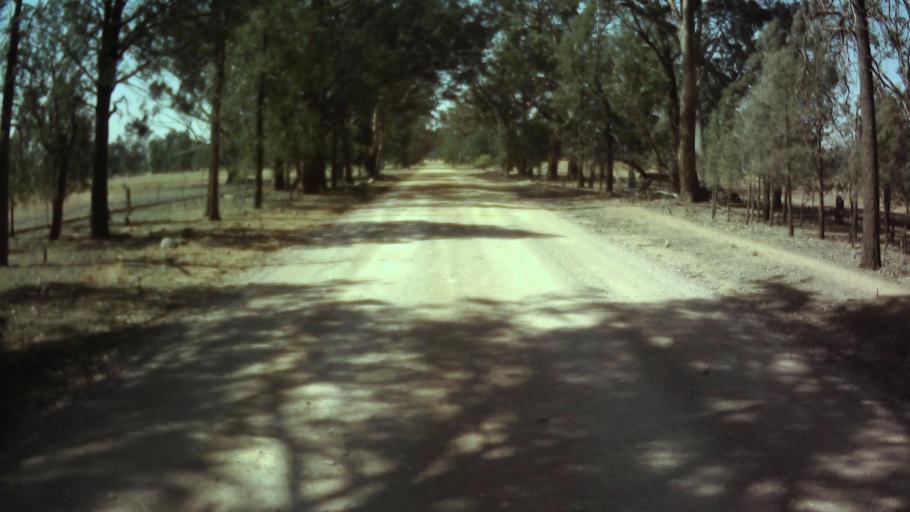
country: AU
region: New South Wales
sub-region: Weddin
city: Grenfell
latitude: -34.0004
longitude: 147.9185
